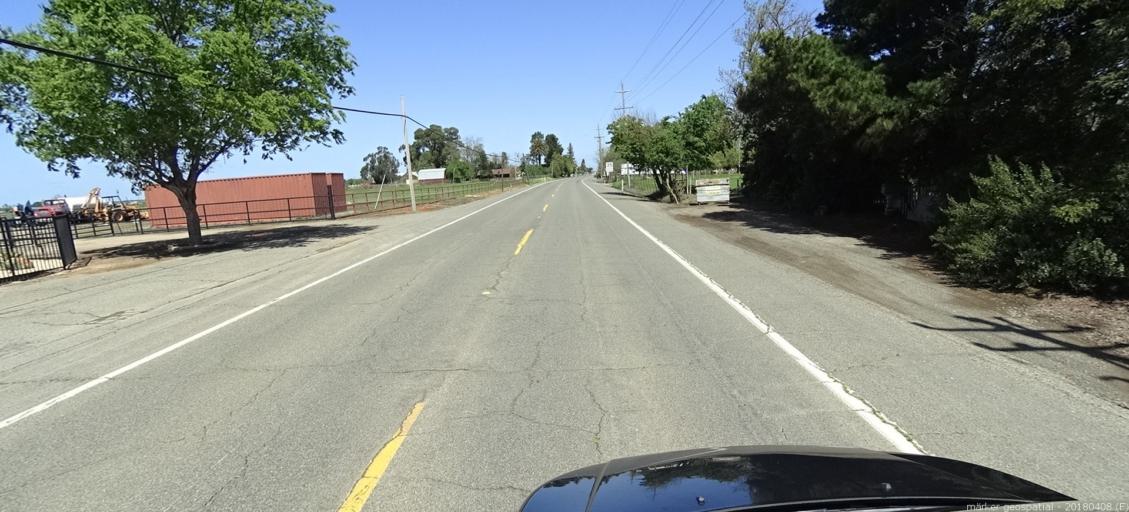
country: US
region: California
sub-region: Sacramento County
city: Laguna
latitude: 38.3706
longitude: -121.4544
